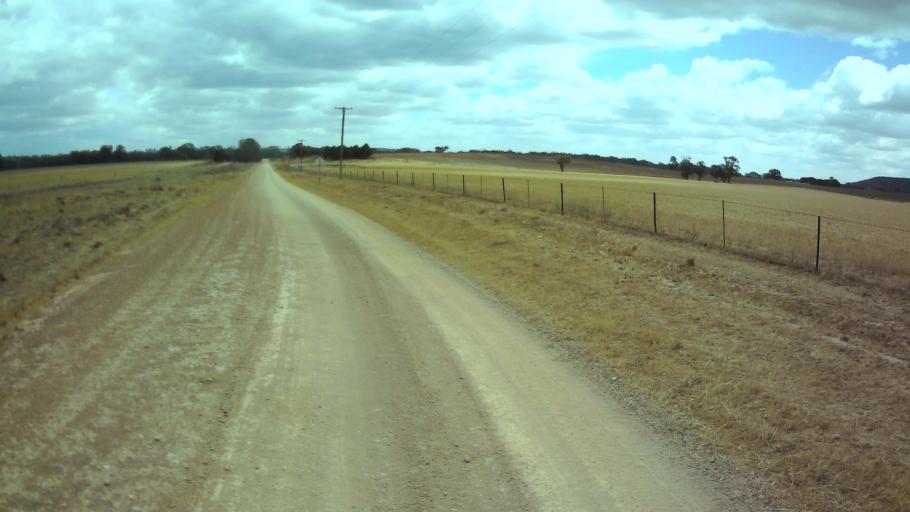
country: AU
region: New South Wales
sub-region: Weddin
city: Grenfell
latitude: -33.9366
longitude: 148.2852
